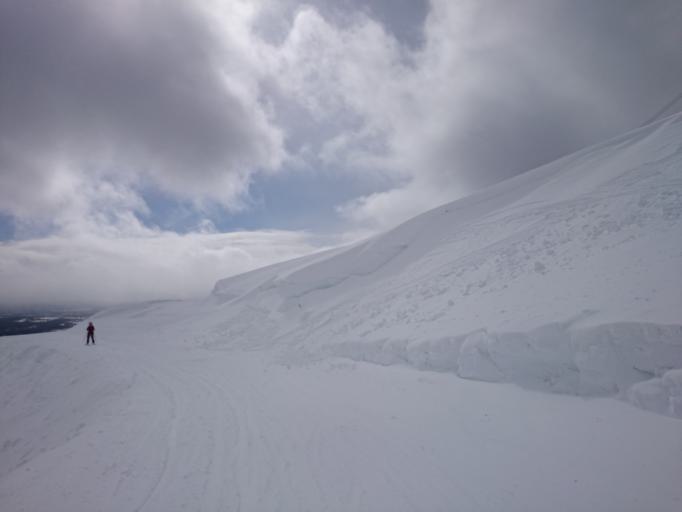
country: SE
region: Jaemtland
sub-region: Are Kommun
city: Are
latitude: 63.4157
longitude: 13.0796
